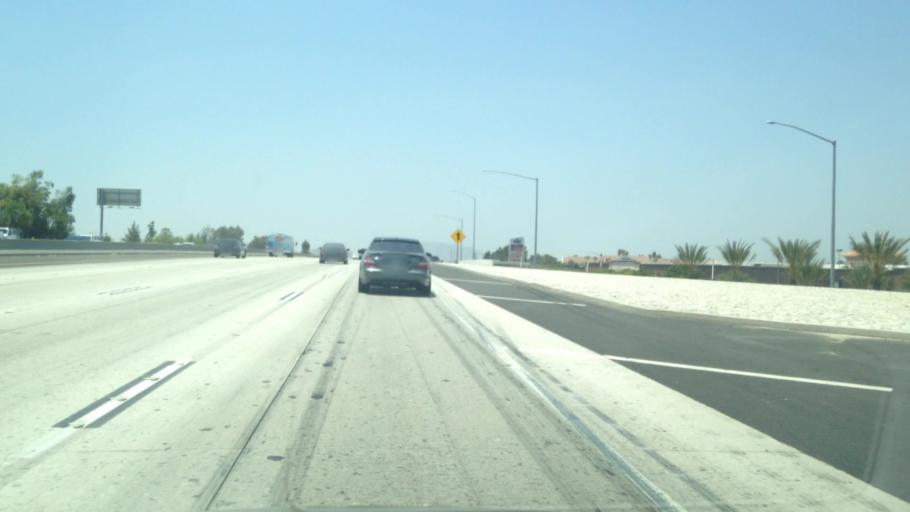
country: US
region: California
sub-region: San Bernardino County
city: Loma Linda
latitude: 34.0650
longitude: -117.2594
